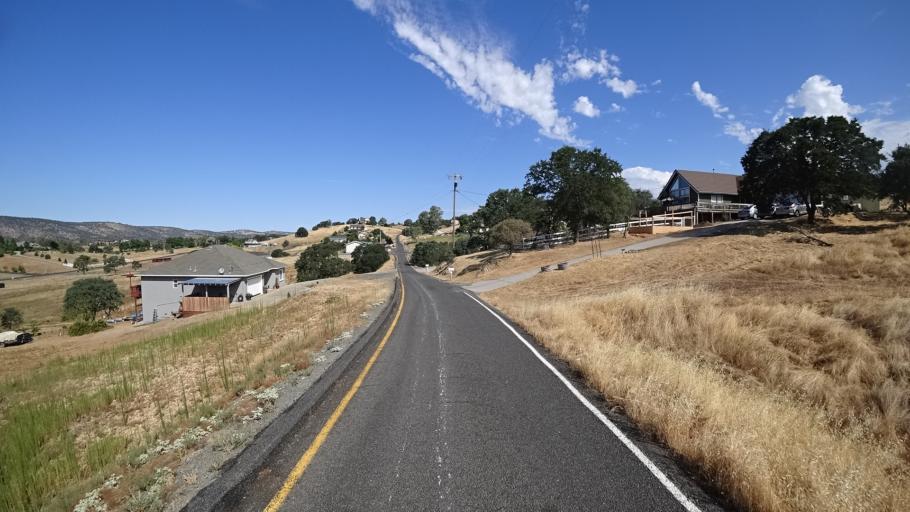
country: US
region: California
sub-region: Calaveras County
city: Copperopolis
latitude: 37.9213
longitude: -120.6280
